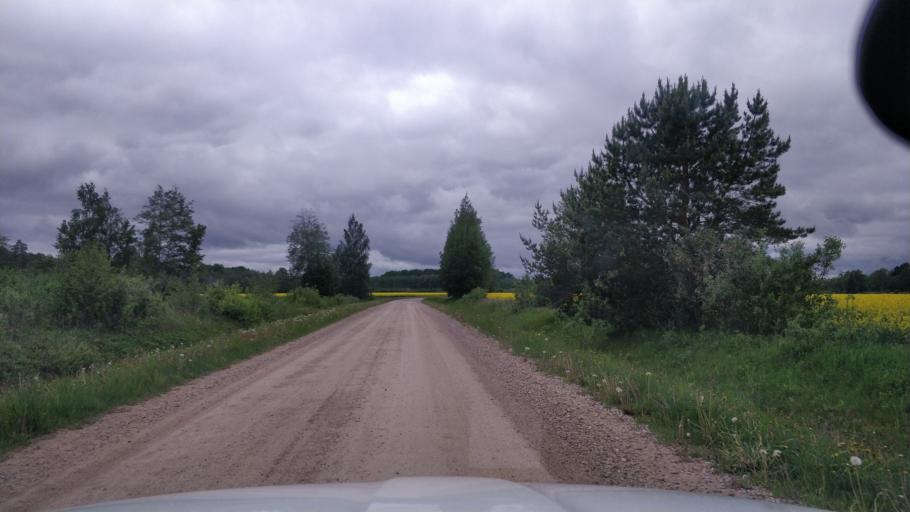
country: EE
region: Paernumaa
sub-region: Halinga vald
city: Parnu-Jaagupi
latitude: 58.7099
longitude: 24.3444
